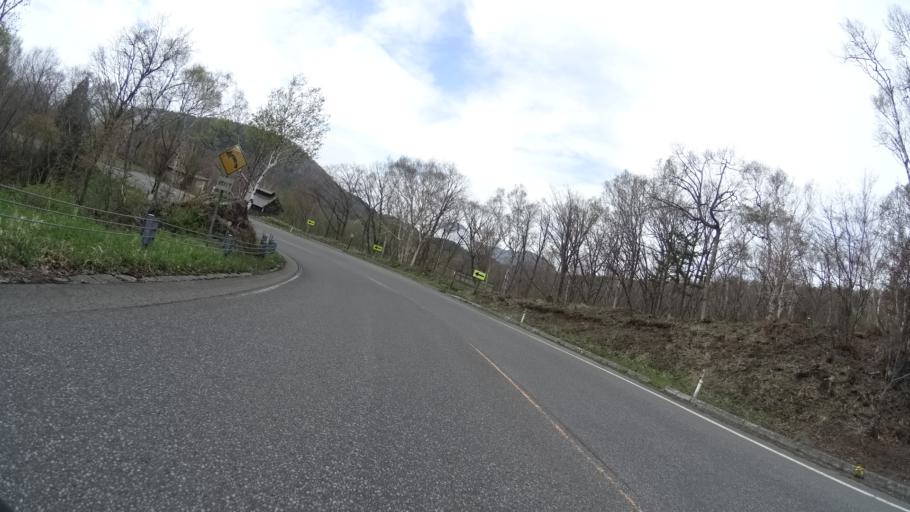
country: JP
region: Nagano
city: Nakano
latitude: 36.7188
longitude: 138.4869
